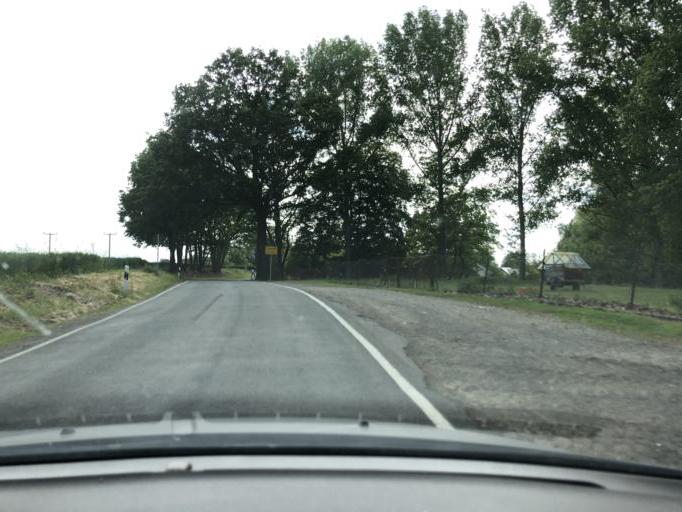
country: DE
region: Saxony
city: Trebsen
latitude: 51.2790
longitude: 12.7301
